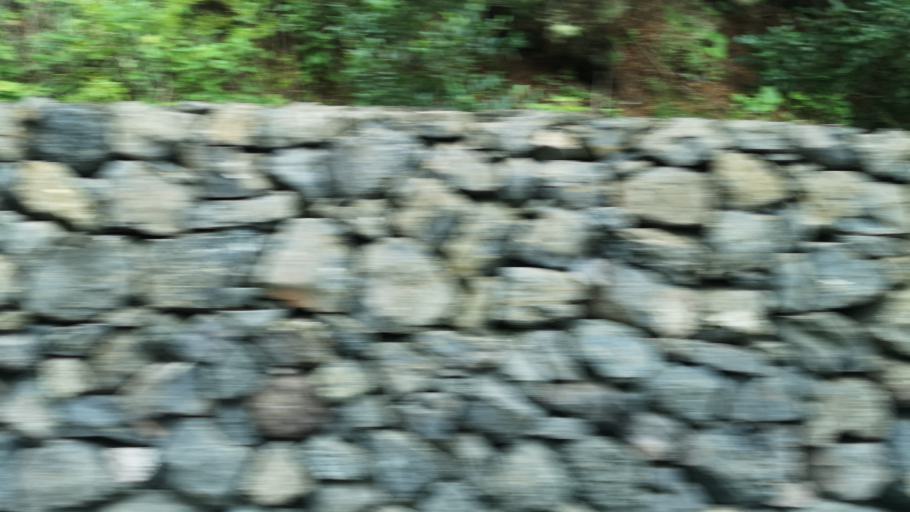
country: ES
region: Canary Islands
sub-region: Provincia de Santa Cruz de Tenerife
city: Hermigua
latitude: 28.1349
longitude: -17.1961
